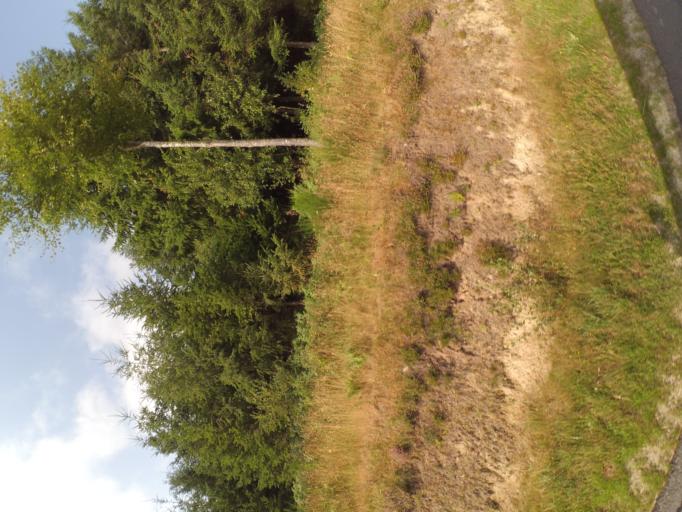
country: FR
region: Limousin
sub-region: Departement de la Correze
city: Meymac
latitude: 45.6023
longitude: 2.1174
